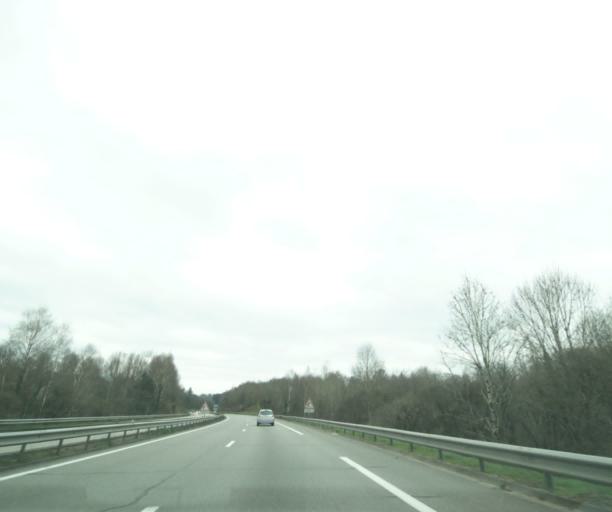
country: FR
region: Limousin
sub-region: Departement de la Haute-Vienne
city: Bonnac-la-Cote
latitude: 45.9325
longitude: 1.3031
